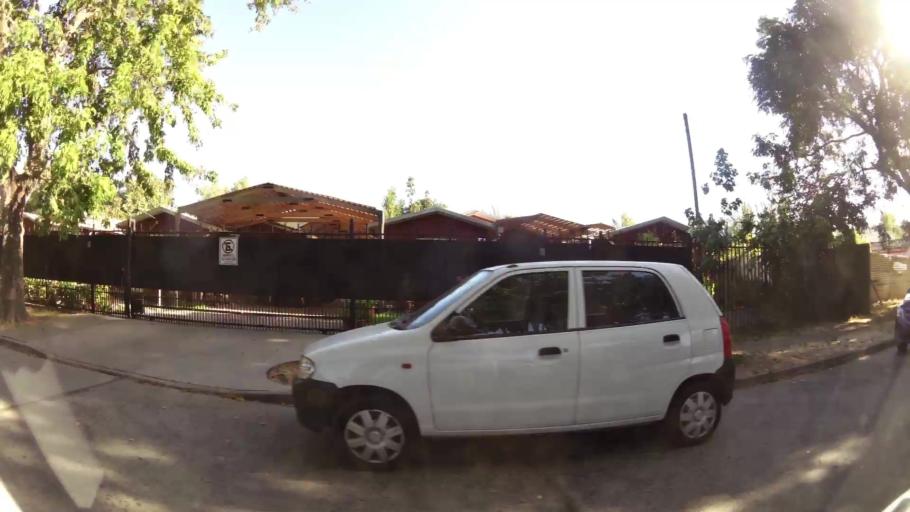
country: CL
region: Maule
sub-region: Provincia de Talca
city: Talca
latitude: -35.4257
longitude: -71.6702
